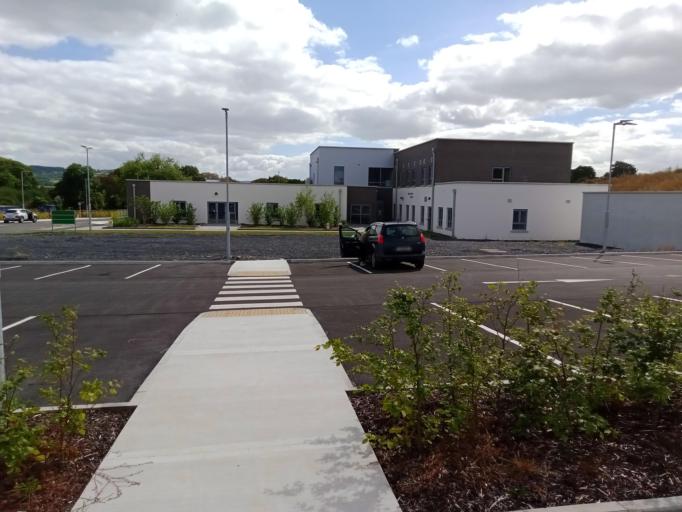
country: IE
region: Leinster
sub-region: Kilkenny
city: Thomastown
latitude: 52.5272
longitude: -7.1439
